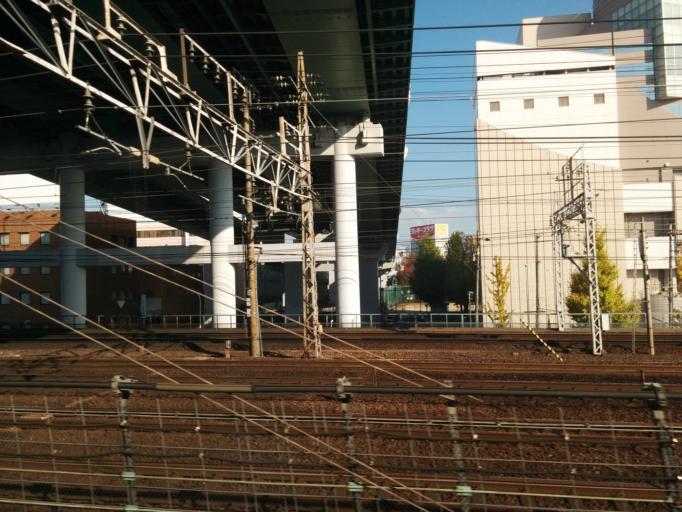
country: JP
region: Aichi
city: Nagoya-shi
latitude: 35.1607
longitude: 136.8860
